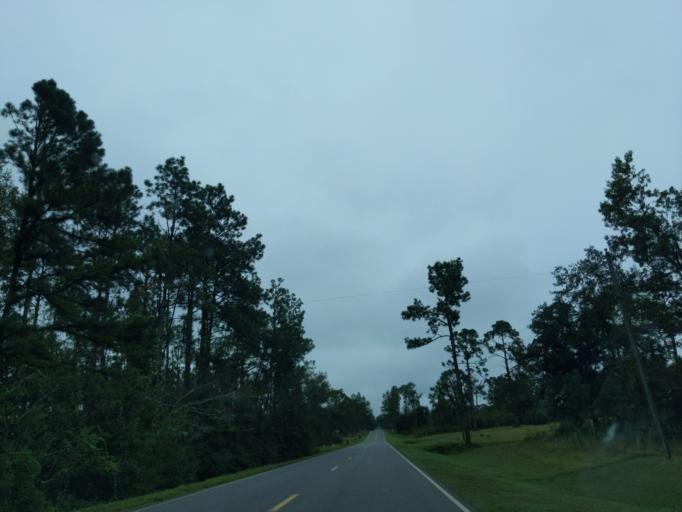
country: US
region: Florida
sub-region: Jackson County
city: Sneads
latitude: 30.7319
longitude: -84.9371
